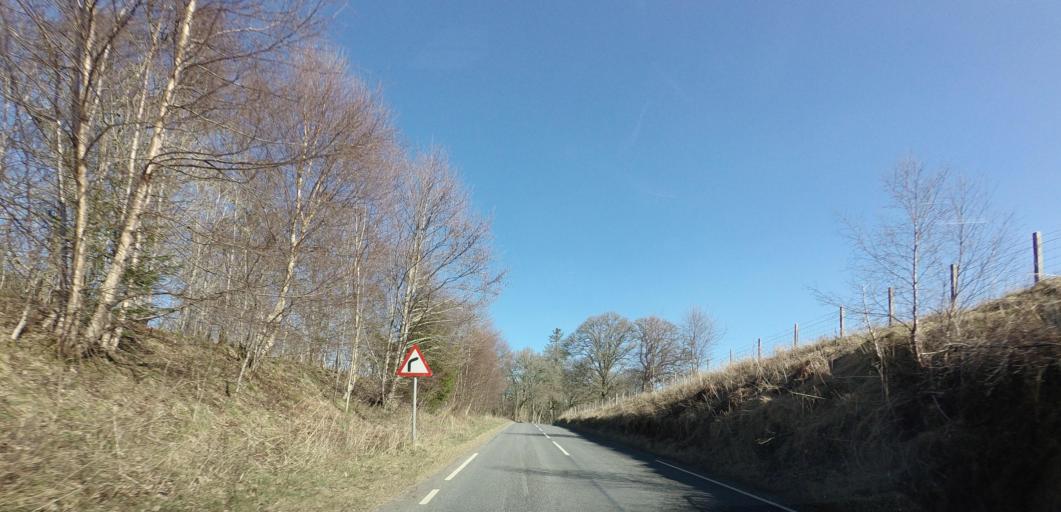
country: GB
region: Scotland
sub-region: Perth and Kinross
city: Bankfoot
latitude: 56.5526
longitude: -3.6290
